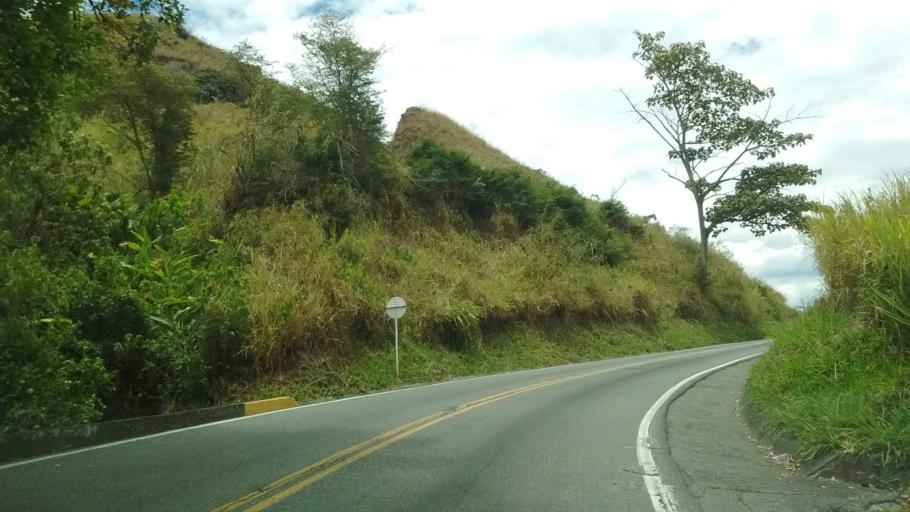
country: CO
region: Cauca
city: La Sierra
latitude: 2.2084
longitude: -76.8009
